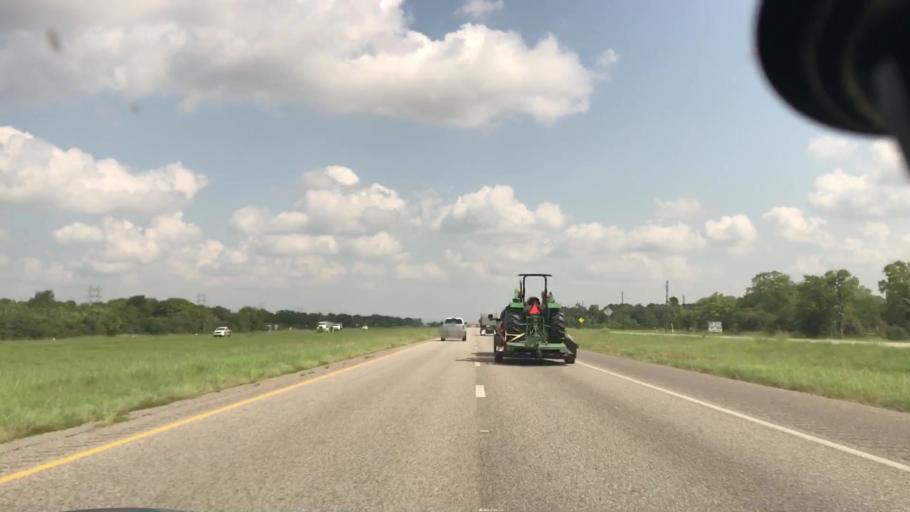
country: US
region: Texas
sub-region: Brazoria County
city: Rosharon
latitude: 29.3887
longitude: -95.4266
